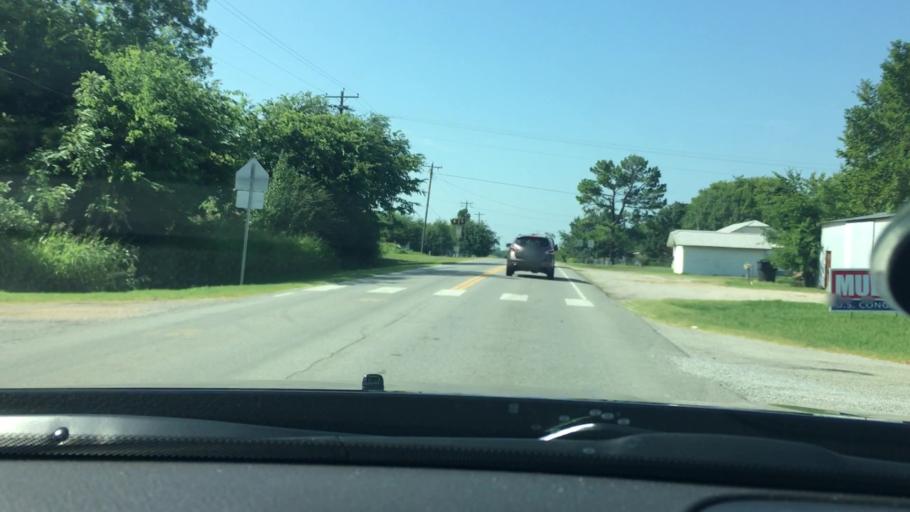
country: US
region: Oklahoma
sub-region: Coal County
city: Coalgate
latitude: 34.6027
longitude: -96.4245
